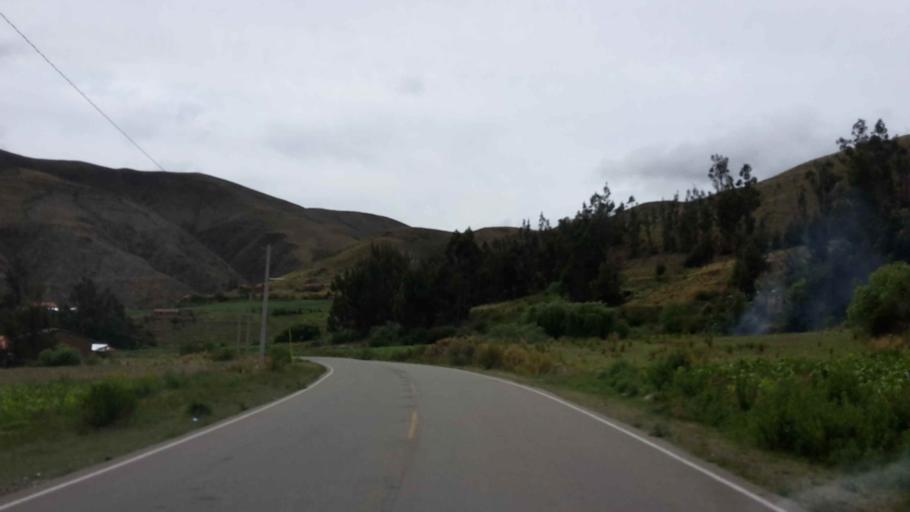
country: BO
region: Cochabamba
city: Colomi
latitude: -17.4091
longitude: -65.7792
